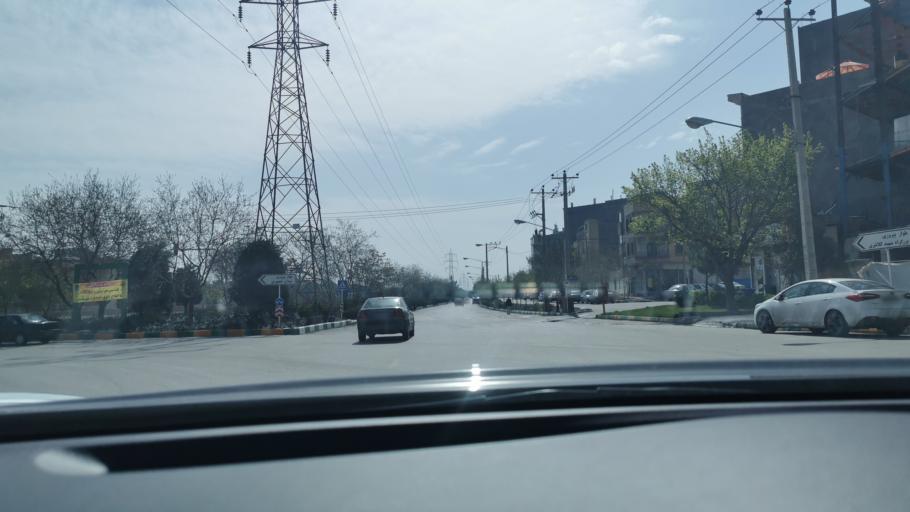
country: IR
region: Razavi Khorasan
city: Mashhad
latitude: 36.2830
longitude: 59.5441
